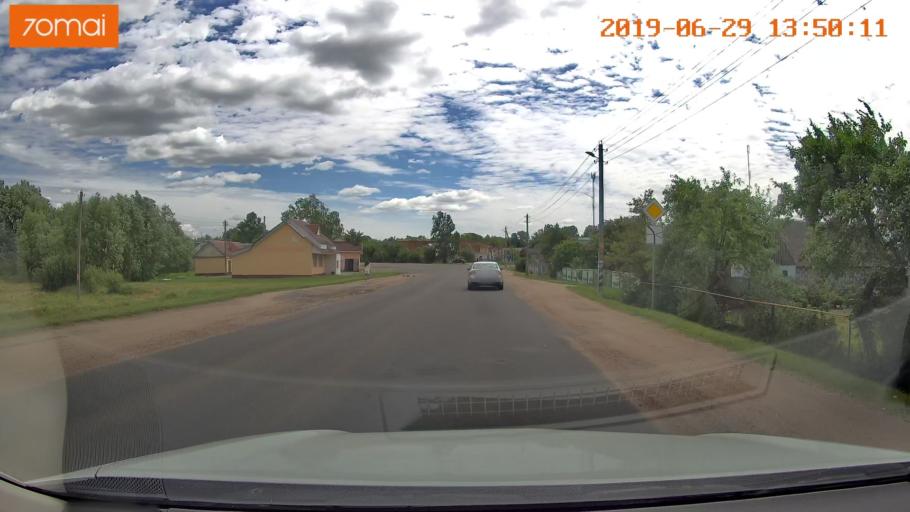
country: BY
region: Minsk
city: Slutsk
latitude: 53.0043
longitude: 27.5669
